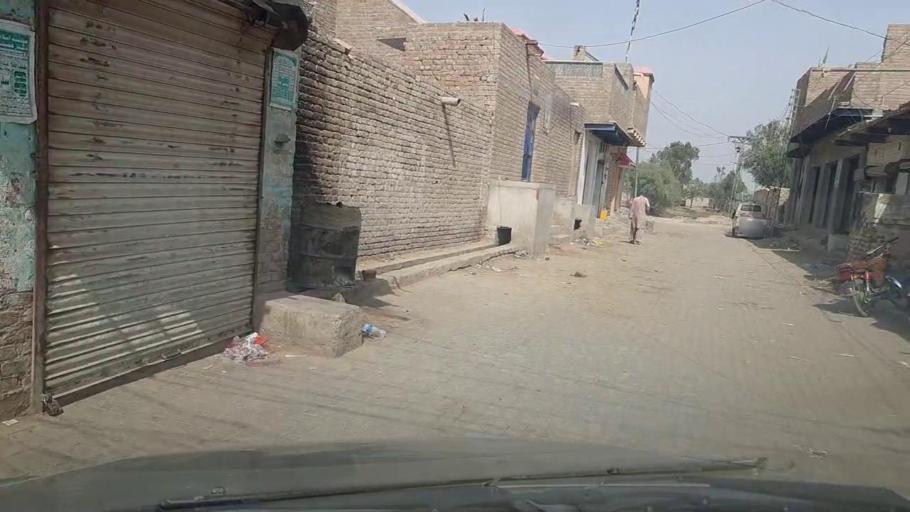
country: PK
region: Sindh
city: Chak
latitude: 27.8305
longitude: 68.7787
